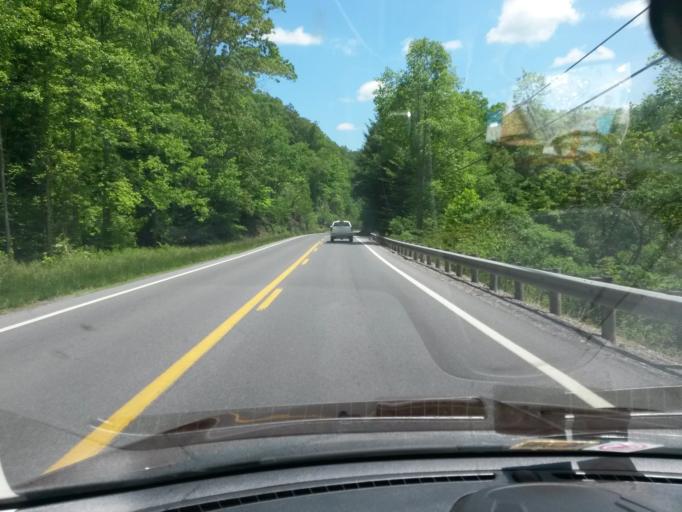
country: US
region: West Virginia
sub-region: Wyoming County
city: Pineville
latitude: 37.5530
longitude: -81.5480
